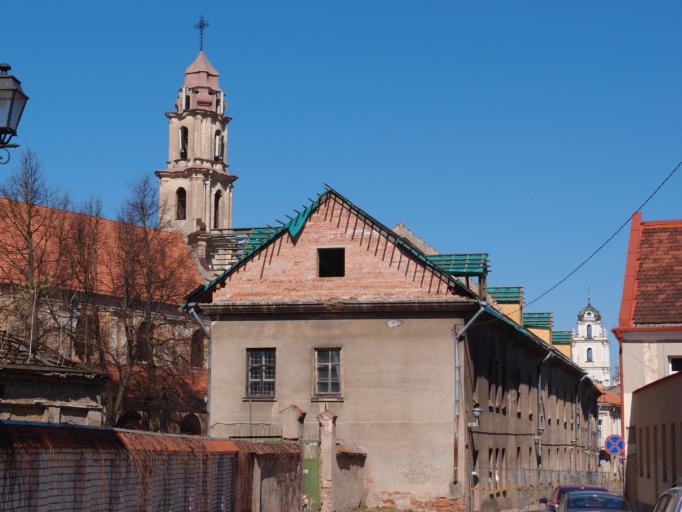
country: LT
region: Vilnius County
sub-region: Vilnius
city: Vilnius
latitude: 54.6777
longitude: 25.2922
